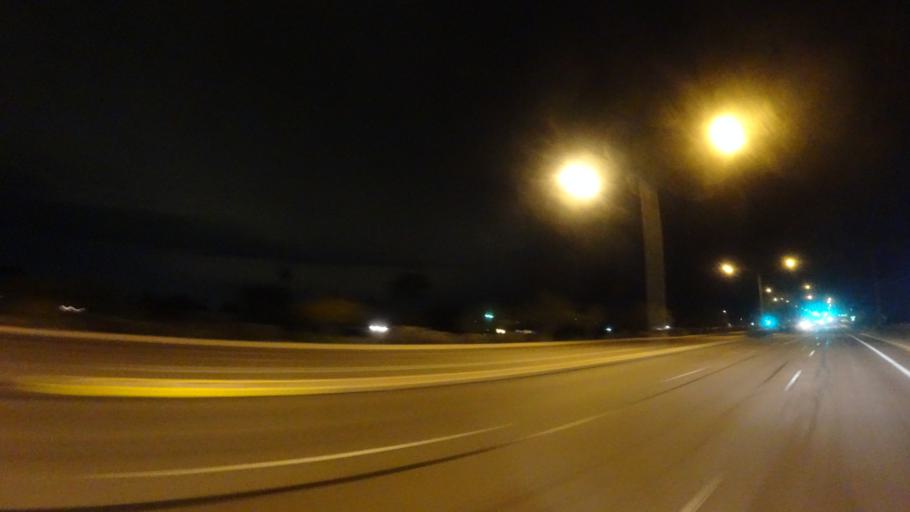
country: US
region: Arizona
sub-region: Pinal County
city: Apache Junction
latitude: 33.4571
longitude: -111.6840
